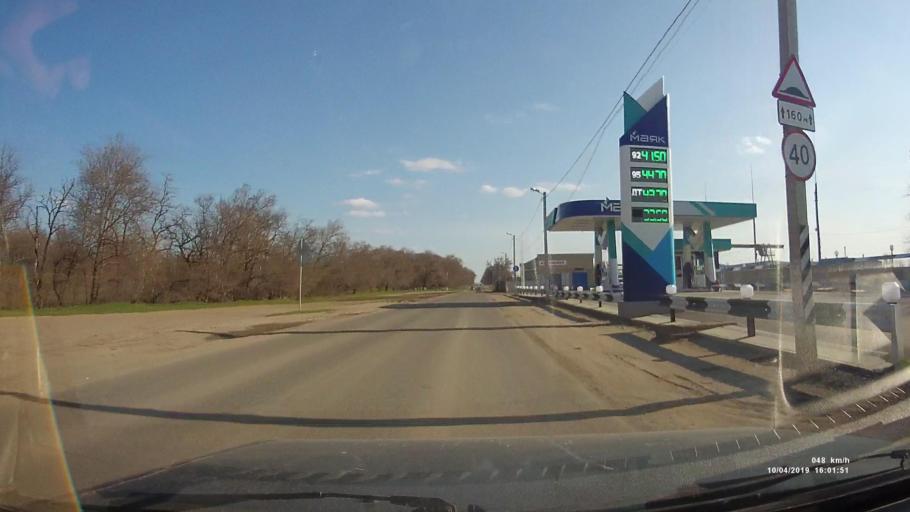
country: RU
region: Rostov
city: Masalovka
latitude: 48.3741
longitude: 40.2618
